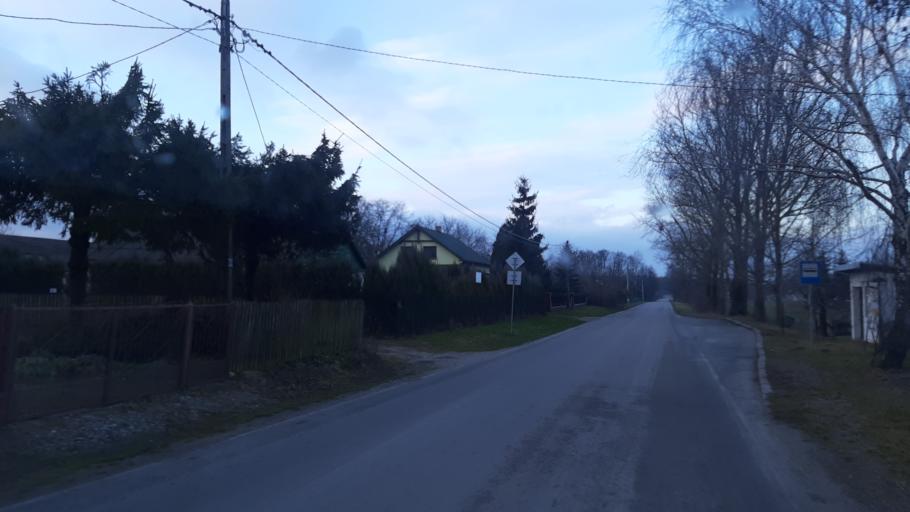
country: PL
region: Lublin Voivodeship
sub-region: Powiat lubelski
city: Jastkow
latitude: 51.3900
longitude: 22.4125
